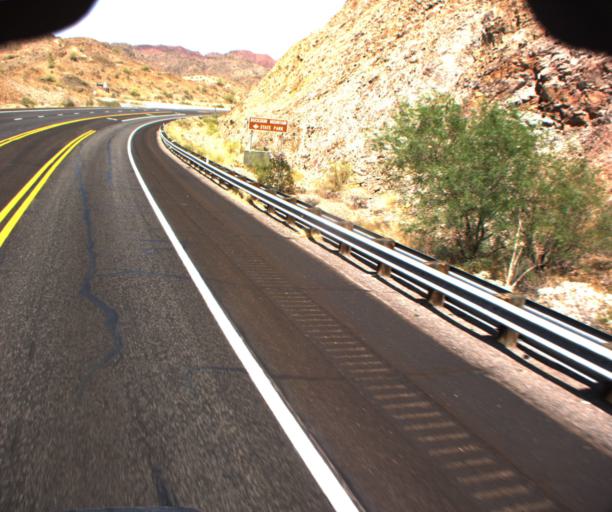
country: US
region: Arizona
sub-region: La Paz County
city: Cienega Springs
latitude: 34.2527
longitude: -114.1618
